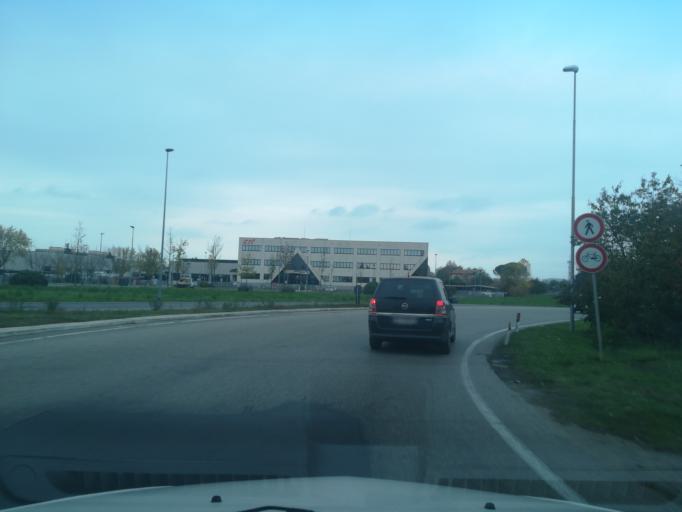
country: IT
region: Emilia-Romagna
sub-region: Provincia di Bologna
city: Imola
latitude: 44.3684
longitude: 11.7033
